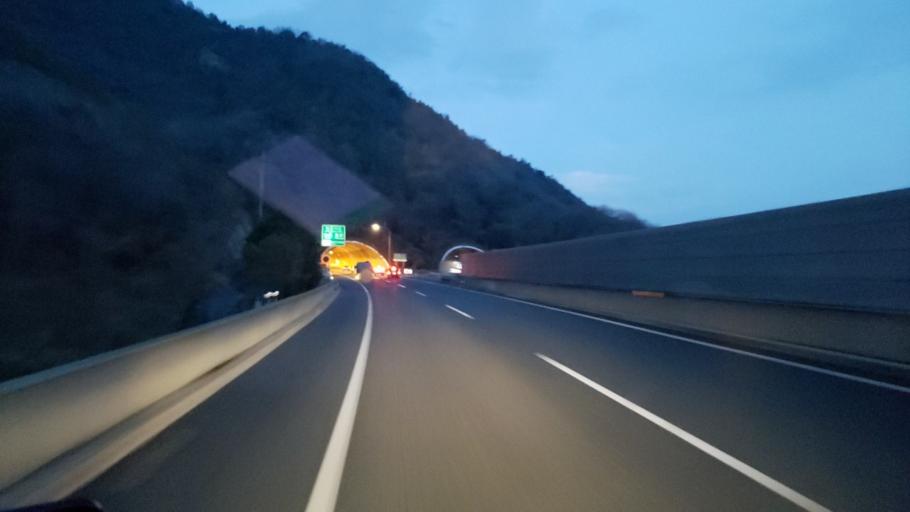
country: JP
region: Hyogo
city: Kakogawacho-honmachi
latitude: 34.8481
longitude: 134.8134
